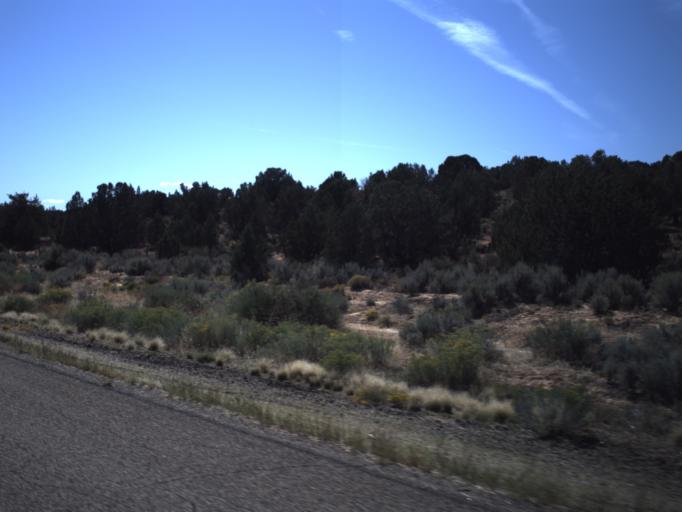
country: US
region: Utah
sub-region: Washington County
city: Ivins
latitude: 37.2683
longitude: -113.6391
